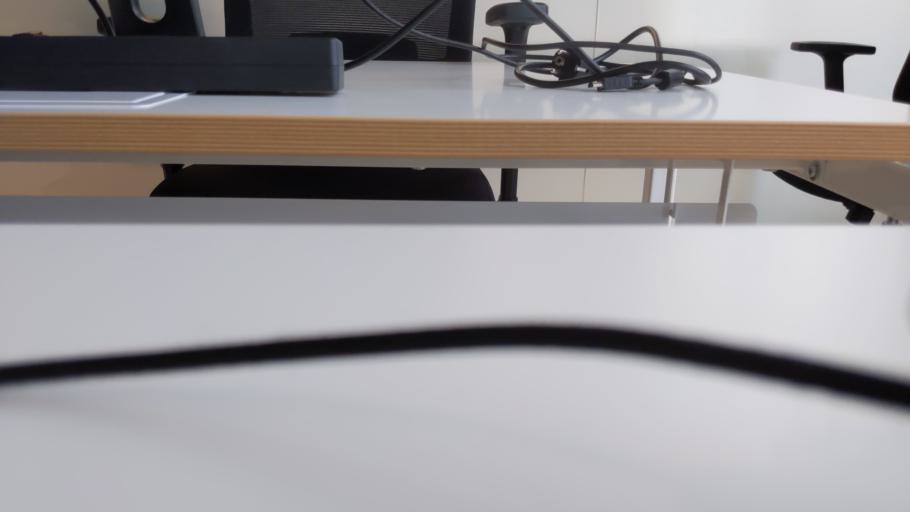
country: RU
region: Moskovskaya
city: Shevlyakovo
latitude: 56.4223
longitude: 36.9972
